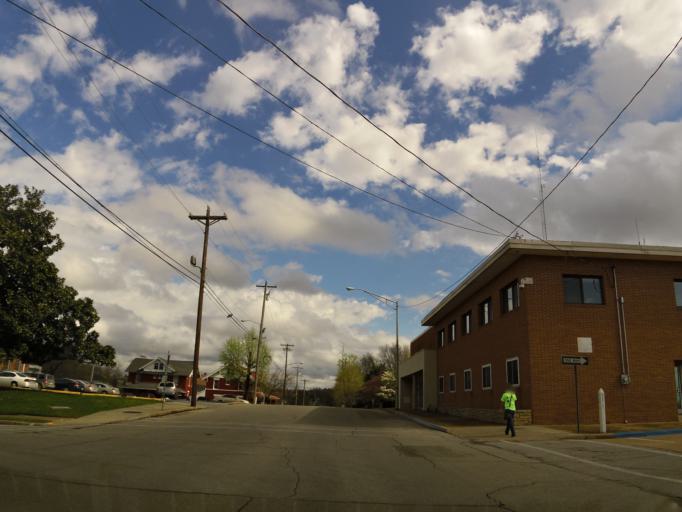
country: US
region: Missouri
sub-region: Butler County
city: Poplar Bluff
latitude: 36.7573
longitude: -90.3918
